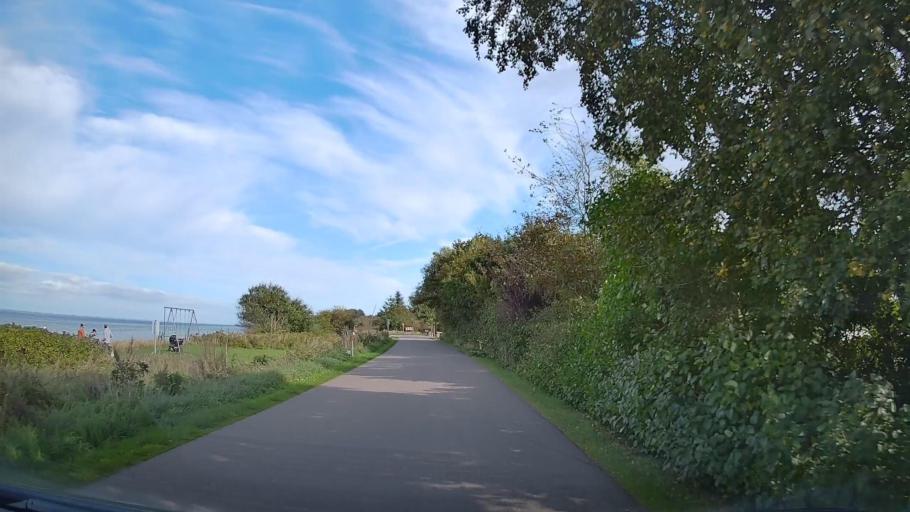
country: DE
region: Schleswig-Holstein
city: Steinberg
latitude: 54.7952
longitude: 9.7736
